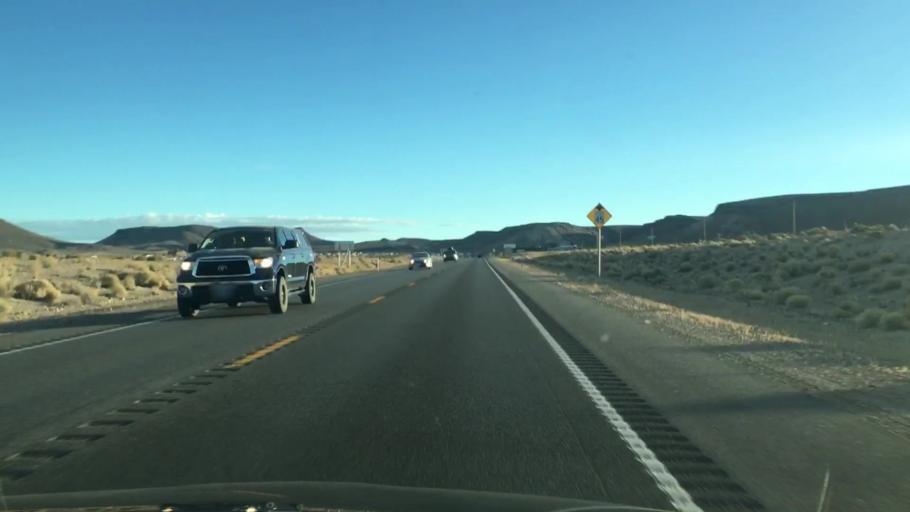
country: US
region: Nevada
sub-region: Esmeralda County
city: Goldfield
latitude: 37.7245
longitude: -117.2436
